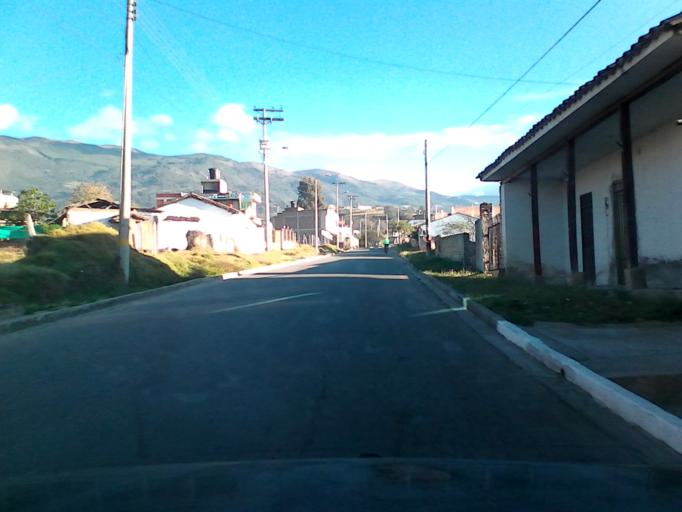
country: CO
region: Boyaca
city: Duitama
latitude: 5.8482
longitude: -73.0264
